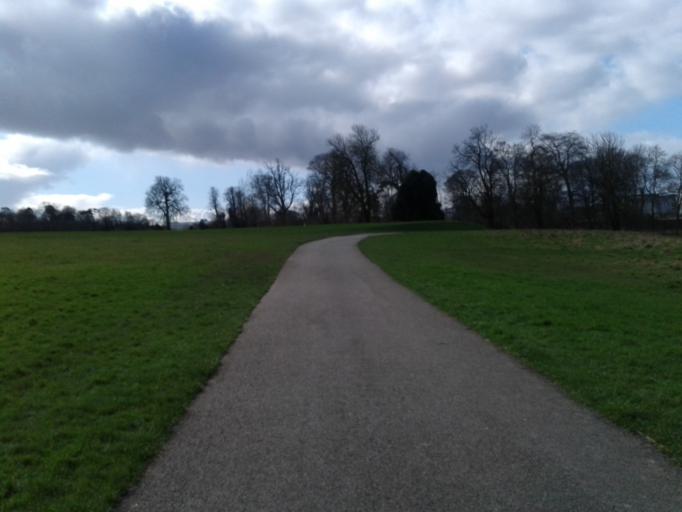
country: IE
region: Leinster
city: Beaumont
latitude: 53.4031
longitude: -6.2469
